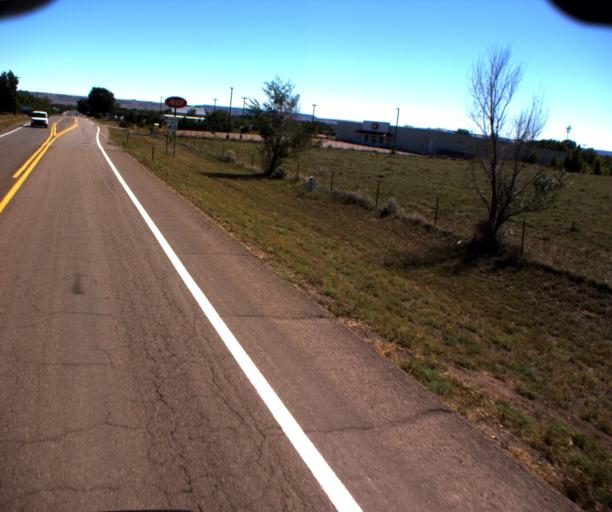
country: US
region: Arizona
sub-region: Apache County
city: Saint Johns
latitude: 34.5063
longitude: -109.3919
